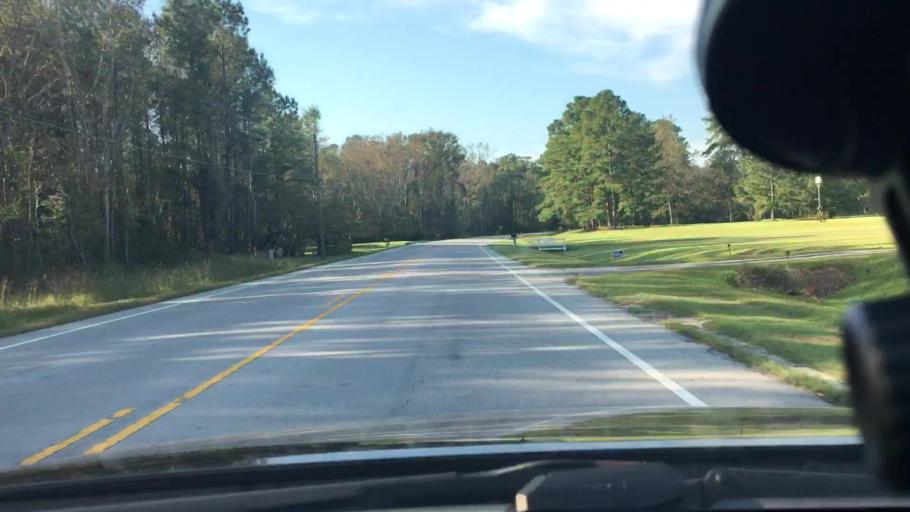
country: US
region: North Carolina
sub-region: Craven County
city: Vanceboro
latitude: 35.2278
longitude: -77.0712
